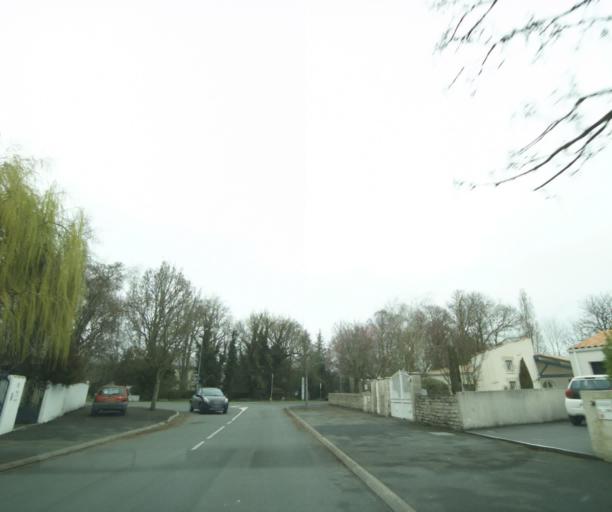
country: FR
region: Poitou-Charentes
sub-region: Departement de la Charente-Maritime
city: Lagord
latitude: 46.1887
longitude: -1.1400
